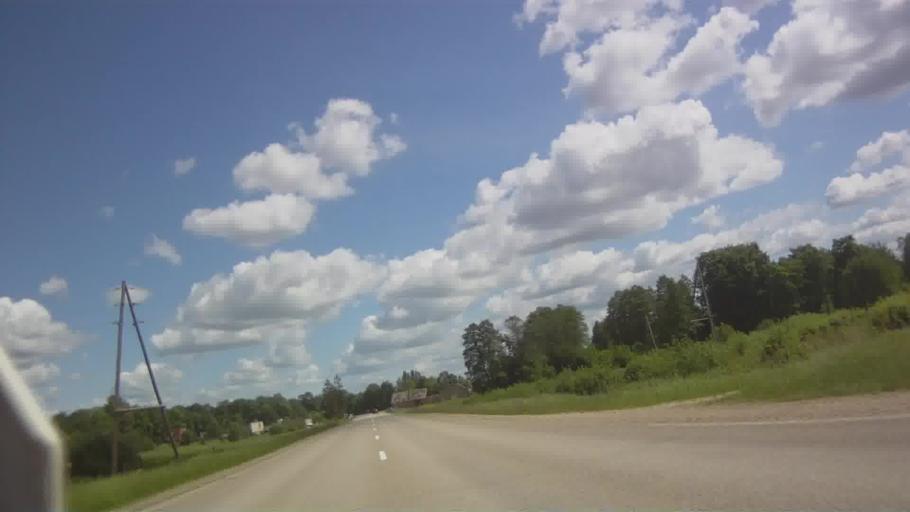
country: LV
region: Varaklani
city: Varaklani
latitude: 56.6033
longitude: 26.7689
